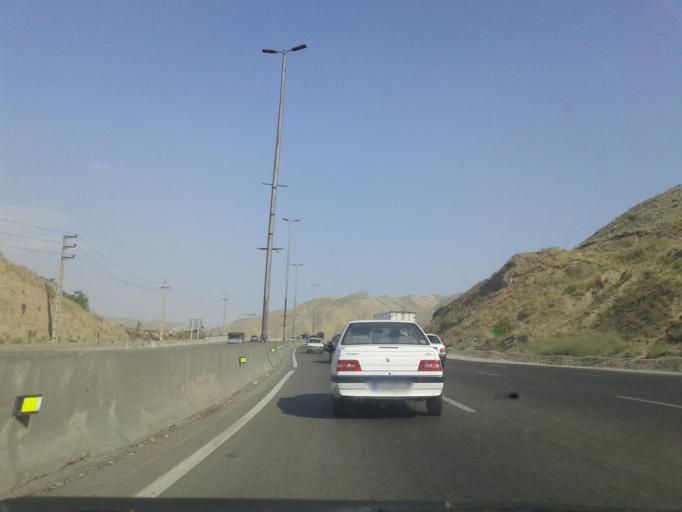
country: IR
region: Tehran
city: Pakdasht
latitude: 35.7334
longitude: 51.6892
